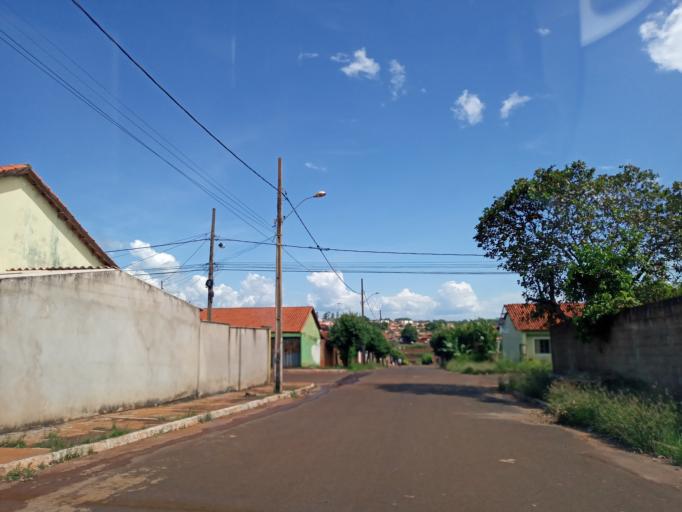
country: BR
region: Goias
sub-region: Itumbiara
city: Itumbiara
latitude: -18.4318
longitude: -49.1848
